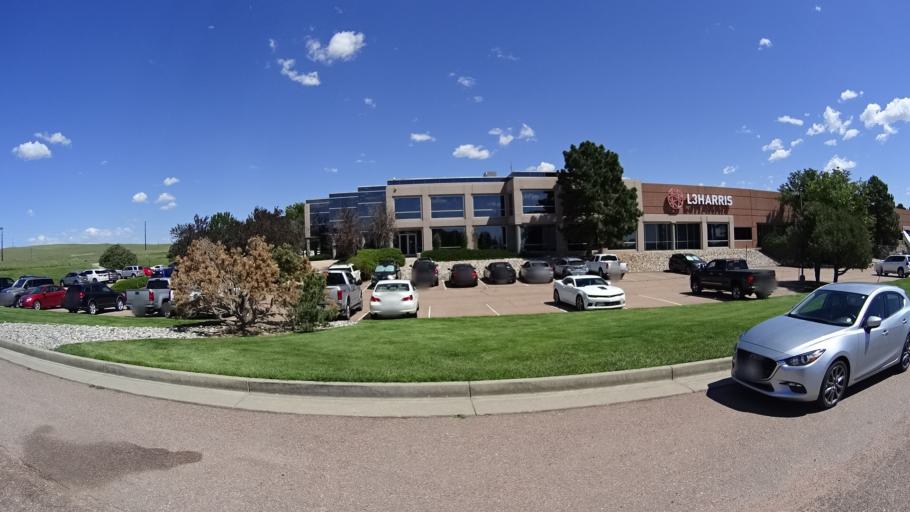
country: US
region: Colorado
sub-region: El Paso County
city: Security-Widefield
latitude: 38.7639
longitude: -104.6688
